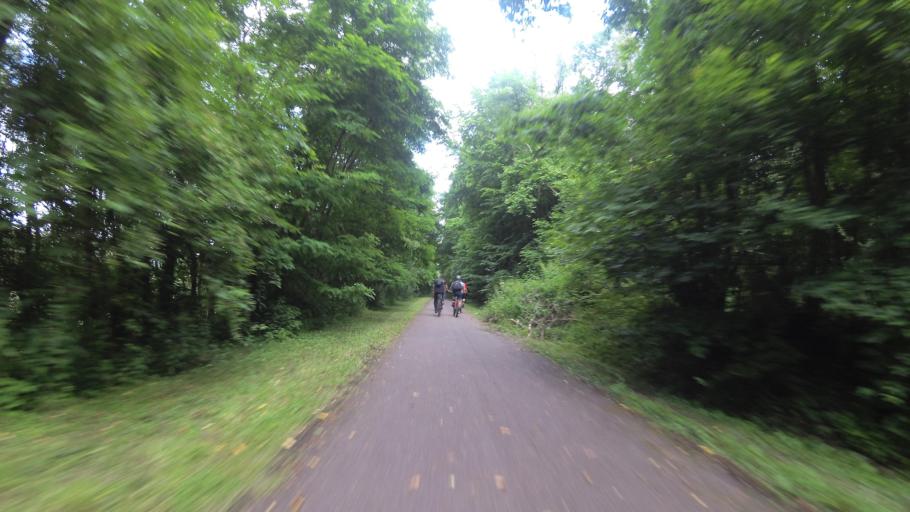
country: FR
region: Lorraine
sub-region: Departement de la Moselle
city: Bliesbruck
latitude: 49.1190
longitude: 7.1570
